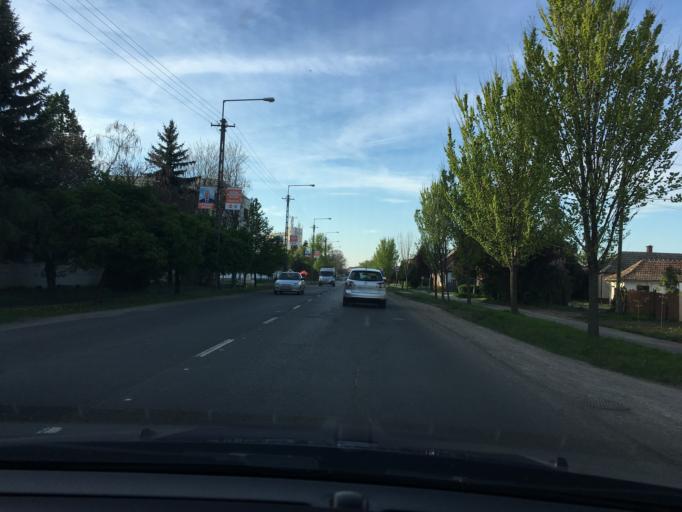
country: HU
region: Hajdu-Bihar
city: Berettyoujfalu
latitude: 47.2122
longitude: 21.5366
